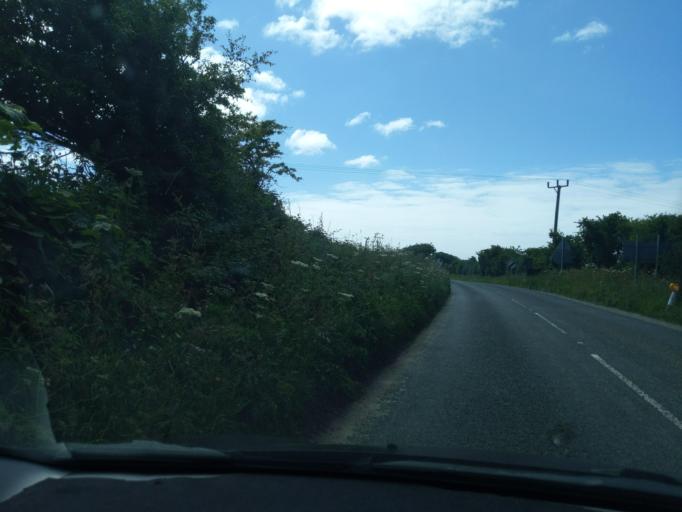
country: GB
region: England
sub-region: Cornwall
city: Perranporth
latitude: 50.2969
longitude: -5.1299
